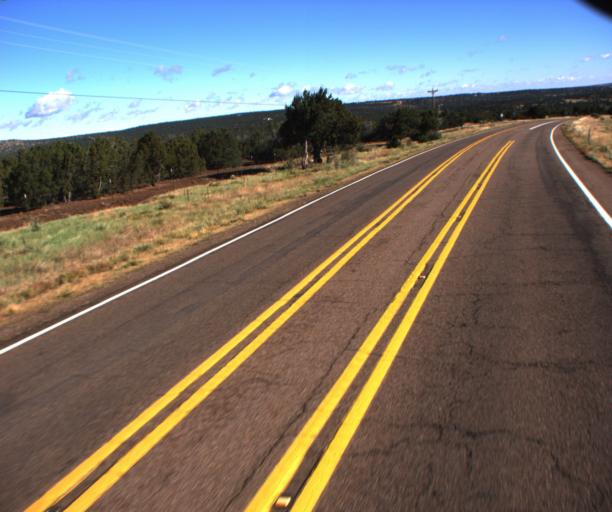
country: US
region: Arizona
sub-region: Navajo County
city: White Mountain Lake
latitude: 34.3154
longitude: -109.7671
